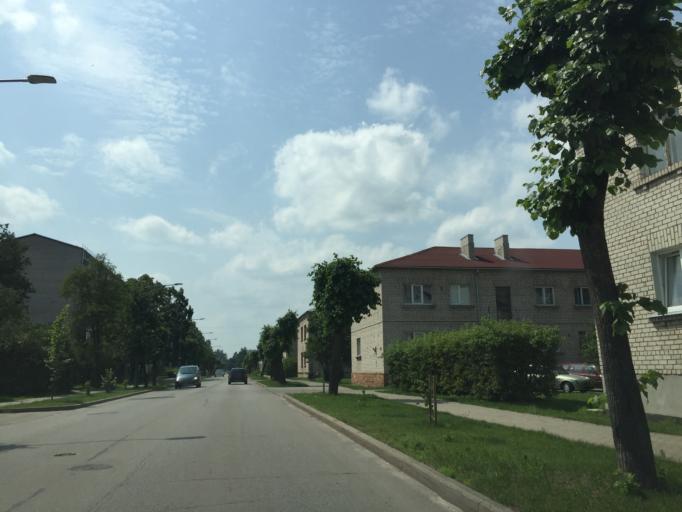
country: LV
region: Olaine
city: Olaine
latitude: 56.7868
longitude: 23.9413
